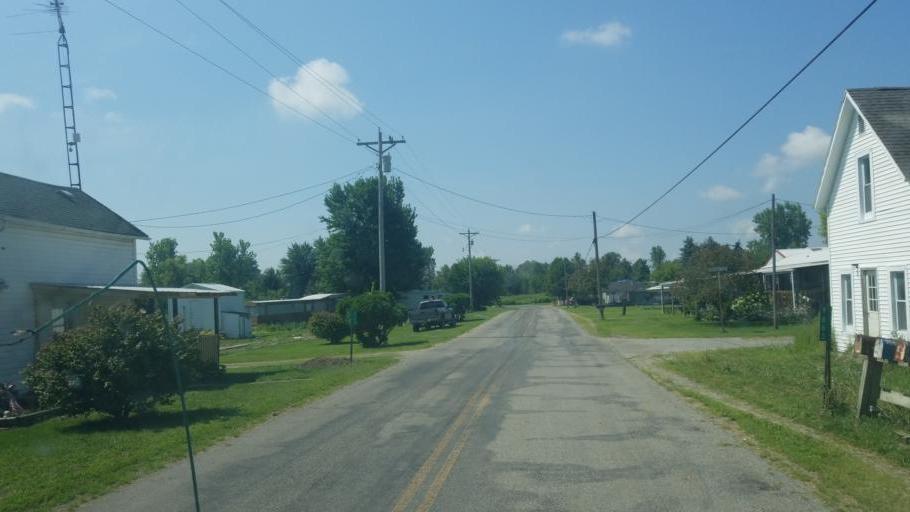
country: US
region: Ohio
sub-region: Hardin County
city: Ada
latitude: 40.6789
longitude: -83.7407
